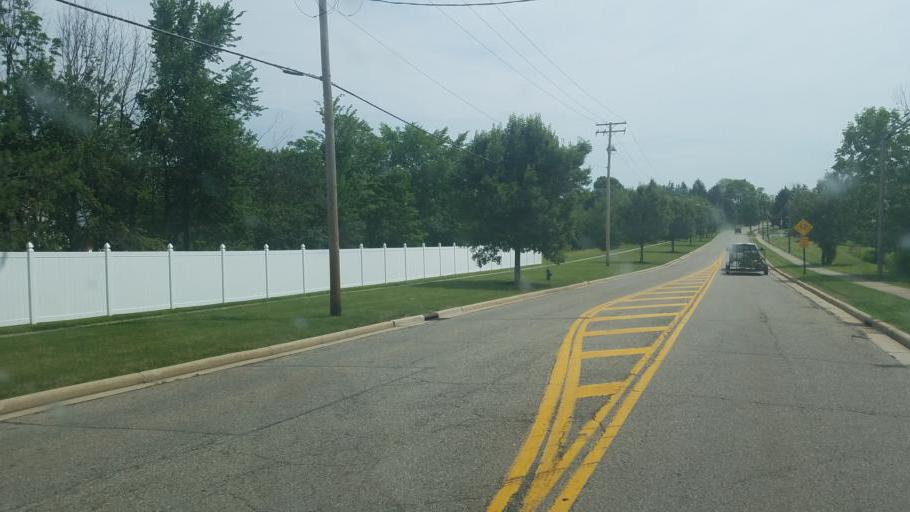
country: US
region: Ohio
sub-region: Summit County
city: Macedonia
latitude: 41.3391
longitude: -81.4755
